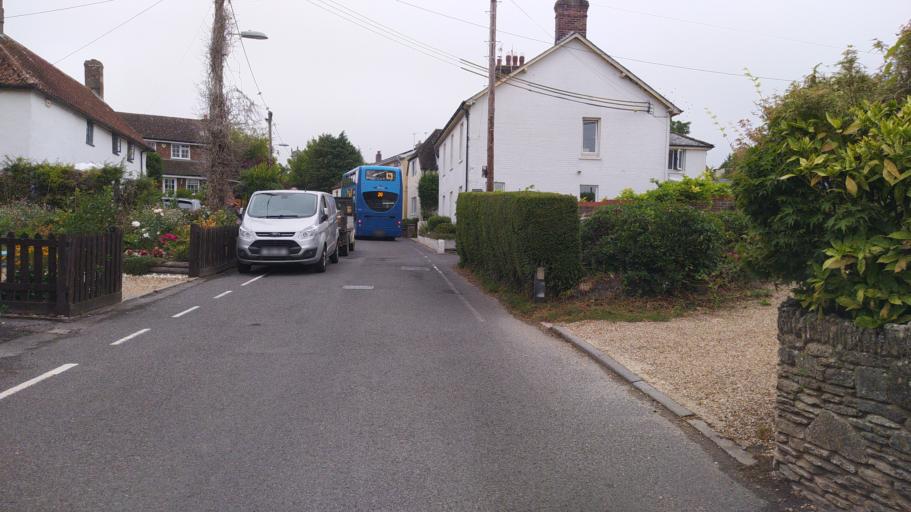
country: GB
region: England
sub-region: Wiltshire
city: Bower Chalke
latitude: 50.9543
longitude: -2.0055
